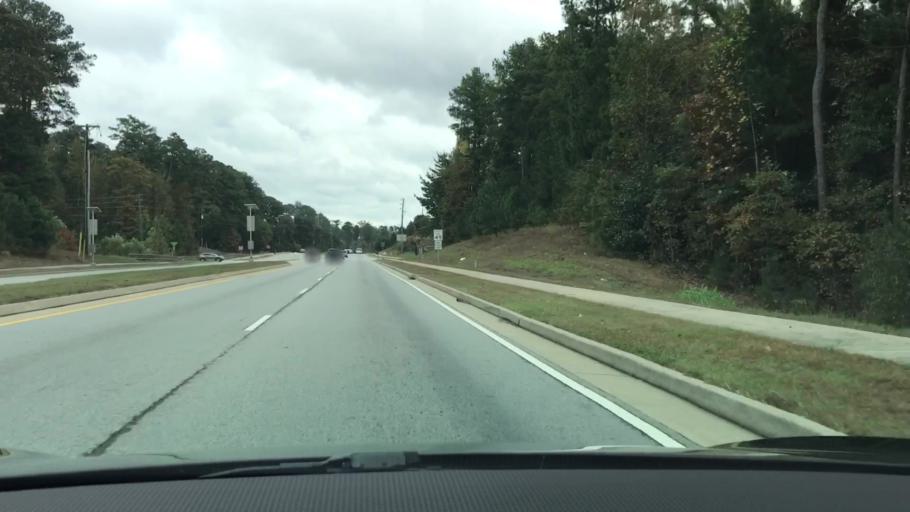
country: US
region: Georgia
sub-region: Gwinnett County
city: Suwanee
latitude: 34.0299
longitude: -84.0614
